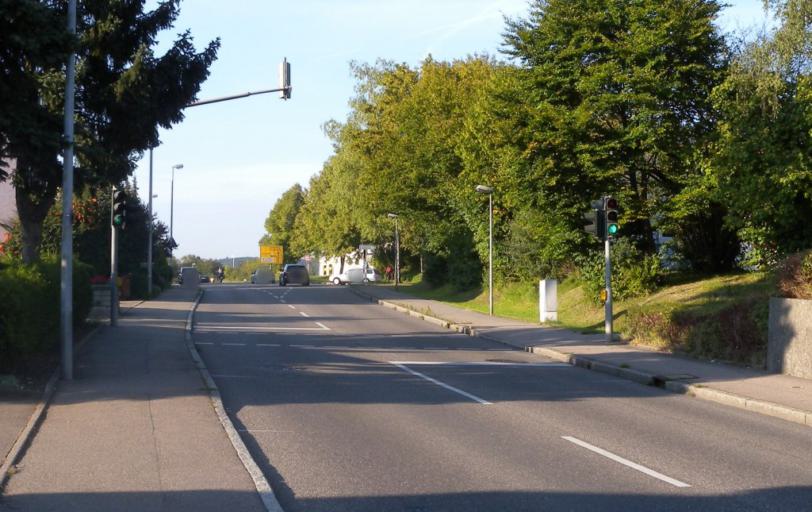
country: DE
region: Baden-Wuerttemberg
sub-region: Regierungsbezirk Stuttgart
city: Schorndorf
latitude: 48.8448
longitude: 9.5402
